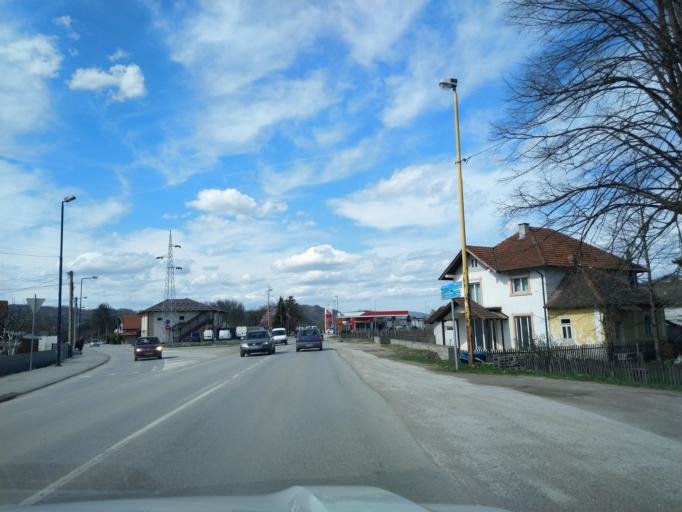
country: RS
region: Central Serbia
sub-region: Zlatiborski Okrug
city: Arilje
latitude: 43.7447
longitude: 20.1068
